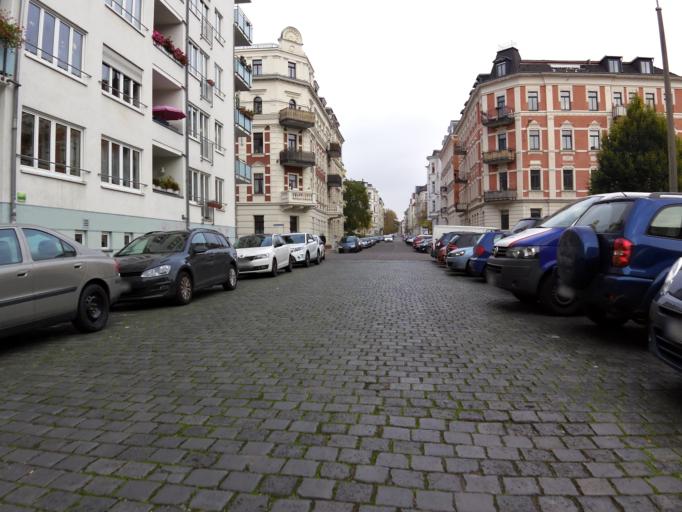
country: DE
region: Saxony
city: Leipzig
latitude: 51.3189
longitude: 12.3668
